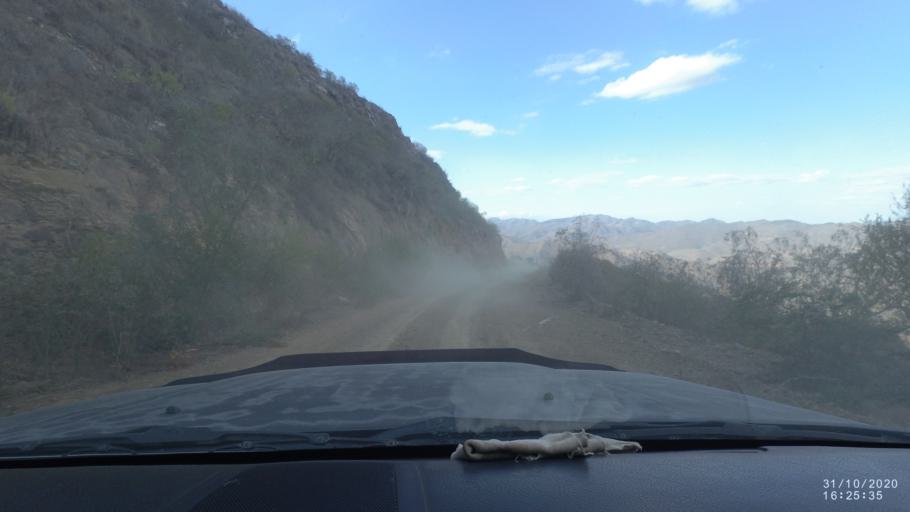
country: BO
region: Chuquisaca
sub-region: Provincia Zudanez
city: Mojocoya
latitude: -18.4000
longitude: -64.5873
